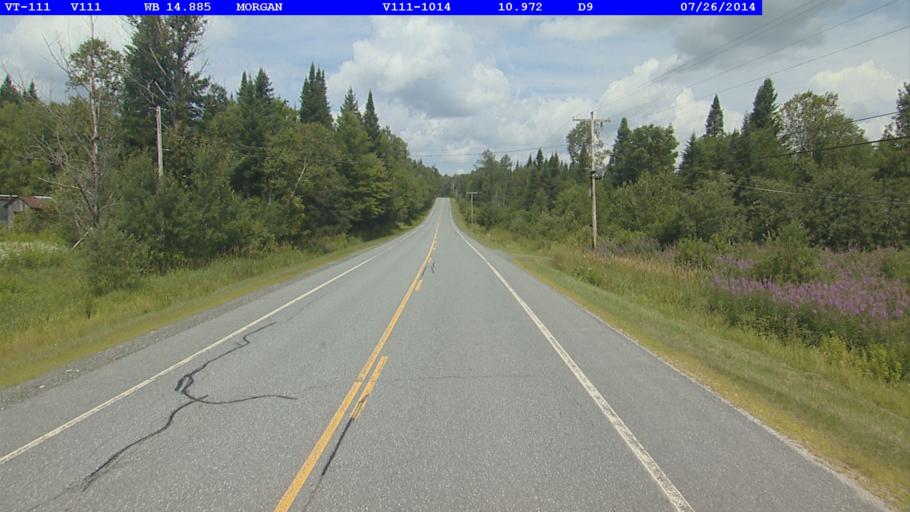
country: US
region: Vermont
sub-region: Orleans County
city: Newport
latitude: 44.8476
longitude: -71.9118
